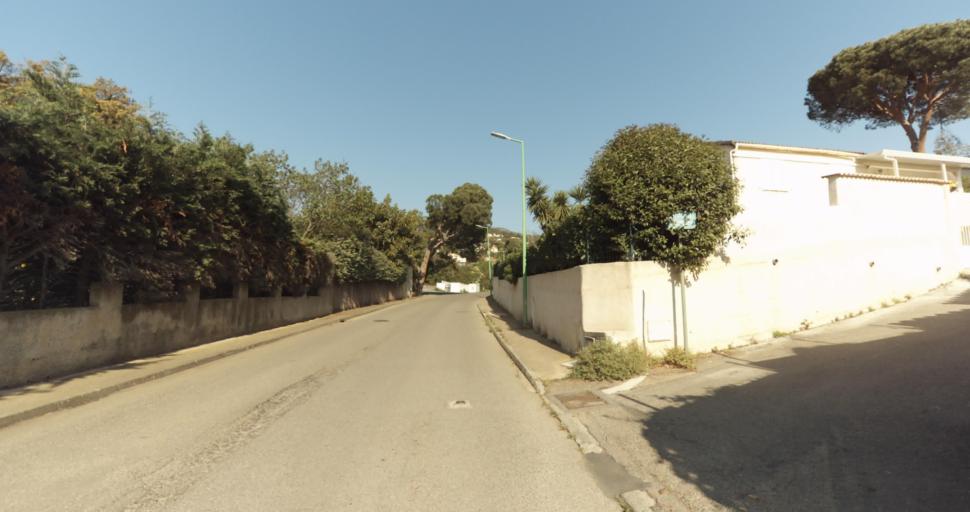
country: FR
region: Corsica
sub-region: Departement de la Haute-Corse
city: Biguglia
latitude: 42.6382
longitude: 9.4298
